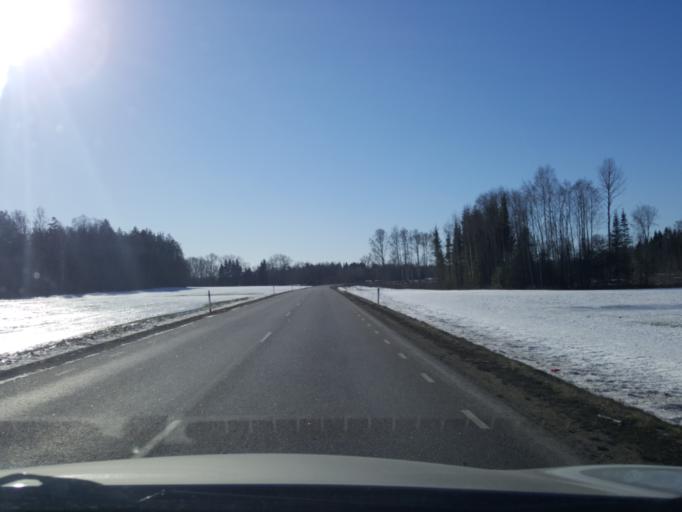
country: EE
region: Viljandimaa
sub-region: Viiratsi vald
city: Viiratsi
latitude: 58.4252
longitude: 25.6828
